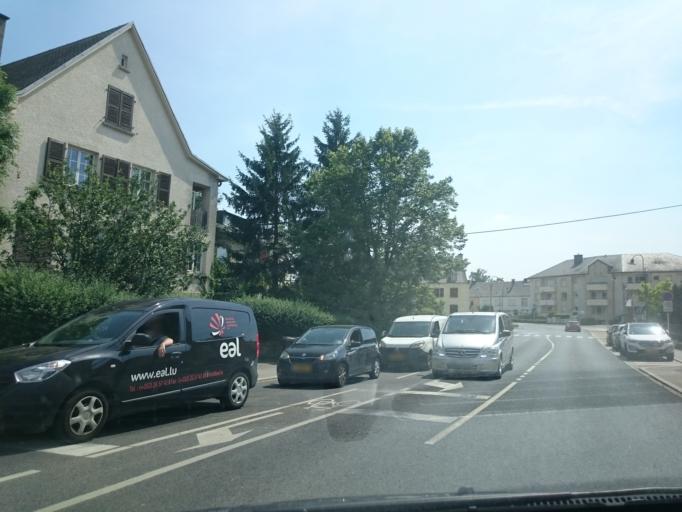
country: LU
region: Luxembourg
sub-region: Canton de Luxembourg
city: Strassen
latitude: 49.6193
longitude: 6.0778
